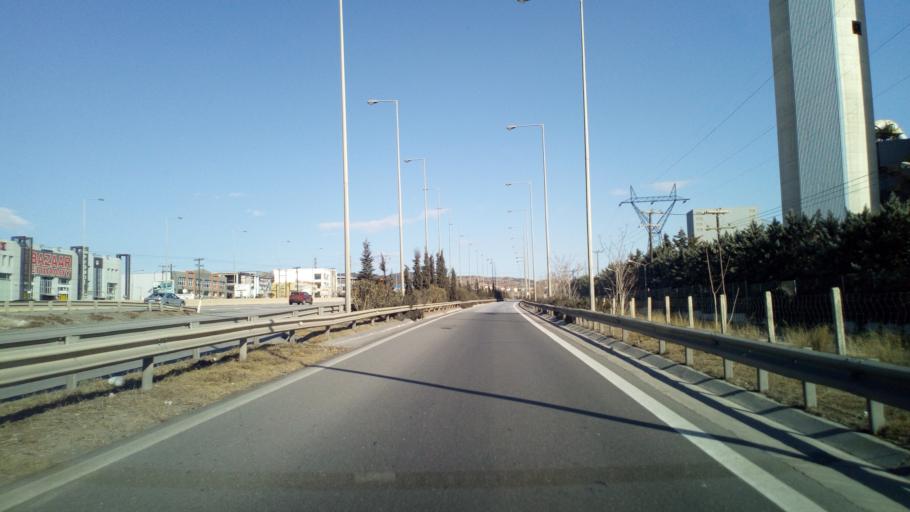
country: GR
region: Central Macedonia
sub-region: Nomos Thessalonikis
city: Efkarpia
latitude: 40.6987
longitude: 22.9497
